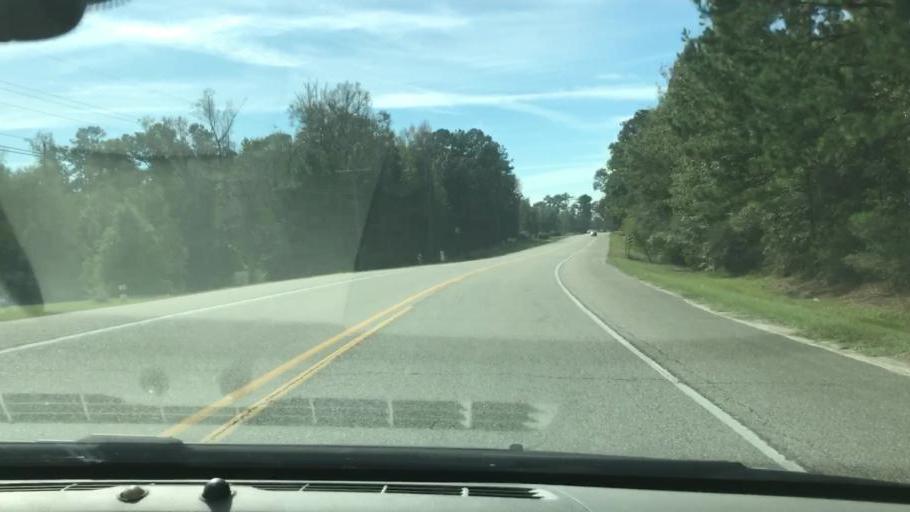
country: US
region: Louisiana
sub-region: Saint Tammany Parish
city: Pearl River
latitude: 30.3896
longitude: -89.7623
